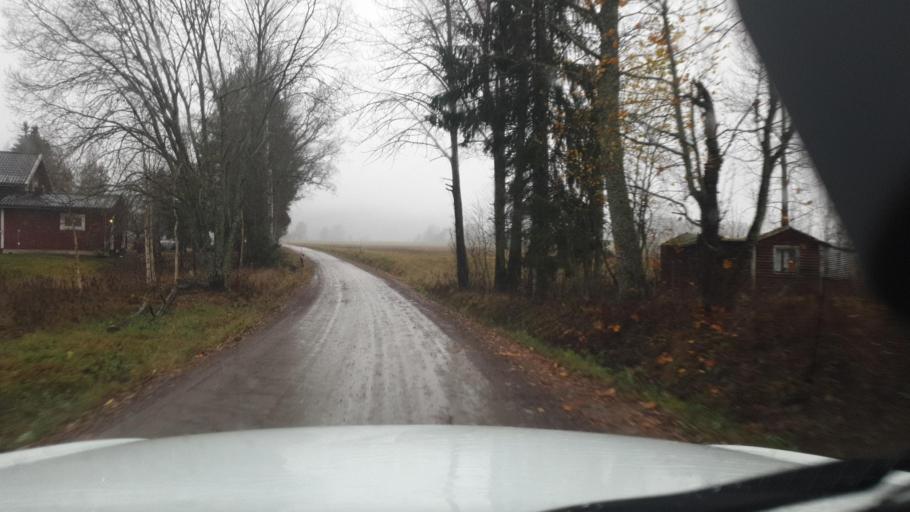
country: SE
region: Vaermland
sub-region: Sunne Kommun
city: Sunne
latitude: 59.8167
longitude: 13.0403
